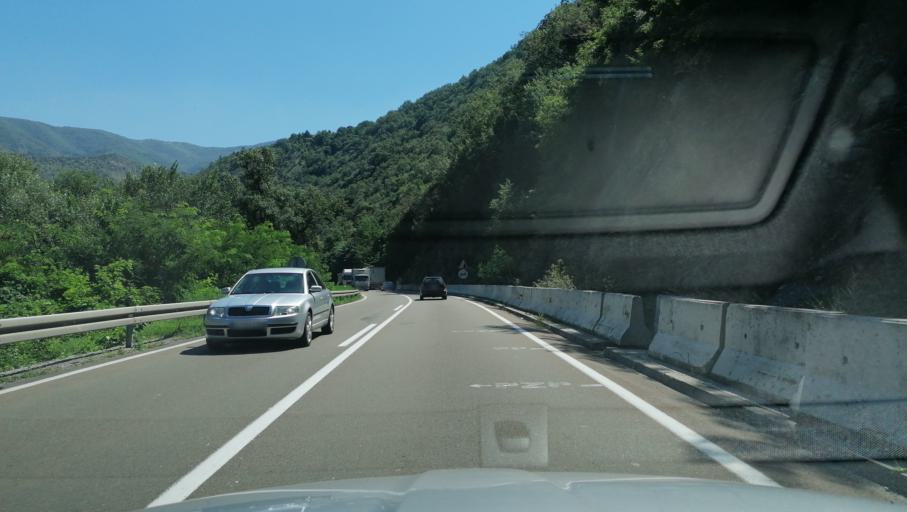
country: RS
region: Central Serbia
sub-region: Raski Okrug
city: Kraljevo
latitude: 43.5629
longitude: 20.6054
